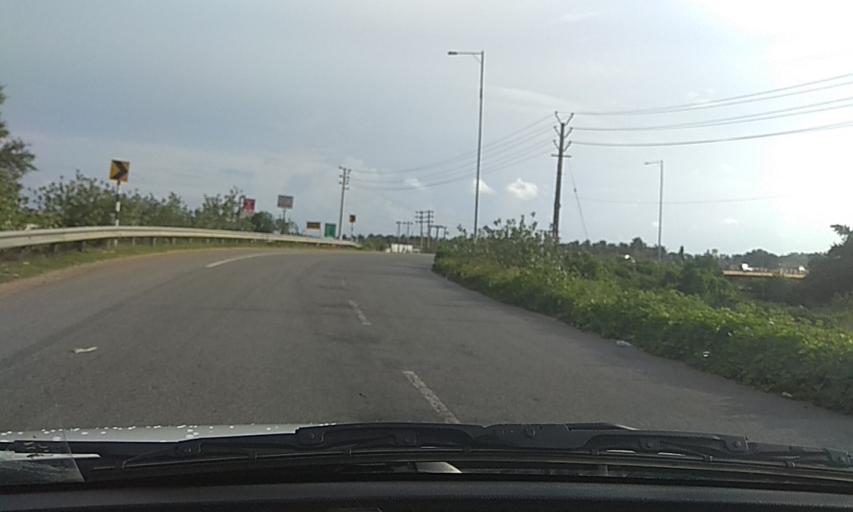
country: IN
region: Karnataka
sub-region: Mysore
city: Nanjangud
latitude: 12.1421
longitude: 76.6770
